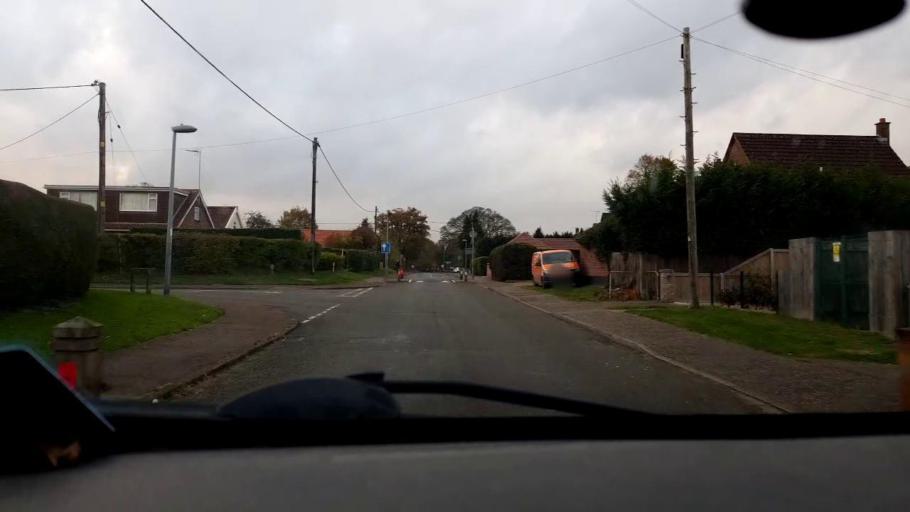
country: GB
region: England
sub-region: Norfolk
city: Spixworth
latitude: 52.6878
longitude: 1.3193
